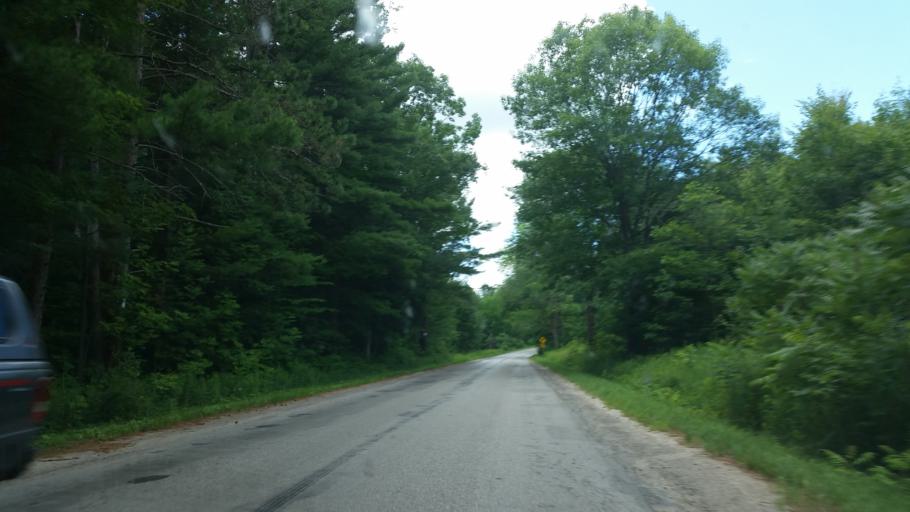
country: CA
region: Ontario
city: Barrie
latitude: 44.4491
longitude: -79.7068
